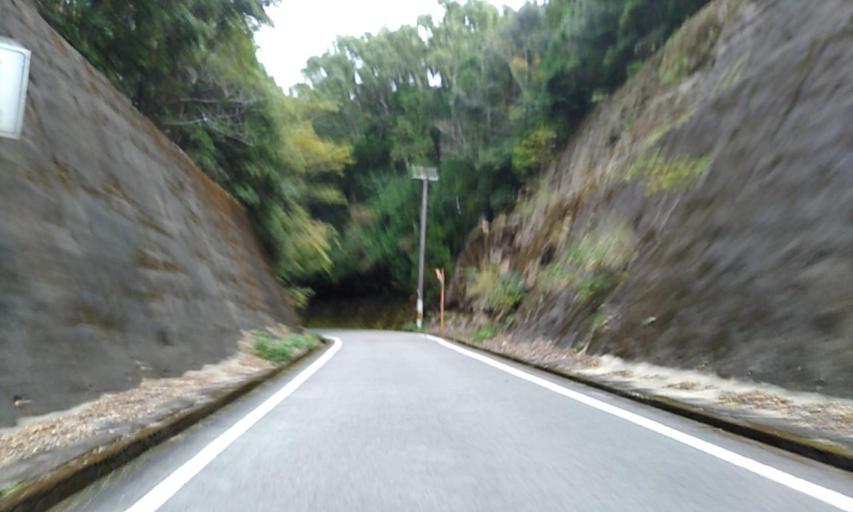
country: JP
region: Wakayama
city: Shingu
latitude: 33.5403
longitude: 135.8365
